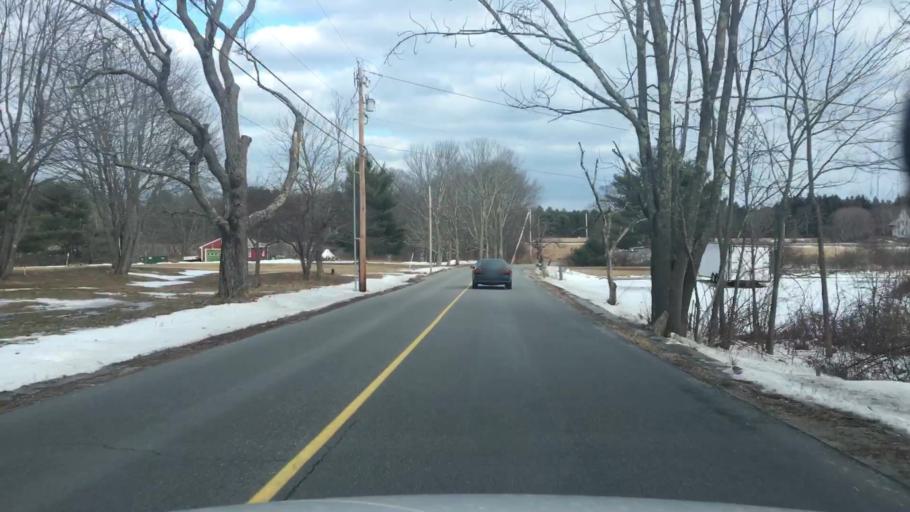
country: US
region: Maine
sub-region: York County
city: Arundel
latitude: 43.4169
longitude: -70.4680
